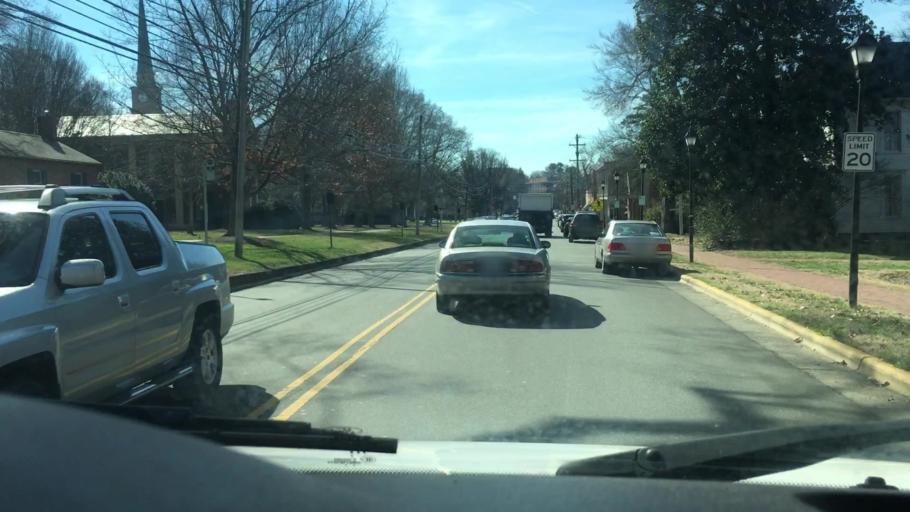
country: US
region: North Carolina
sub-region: Gaston County
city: Davidson
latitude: 35.5014
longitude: -80.8476
